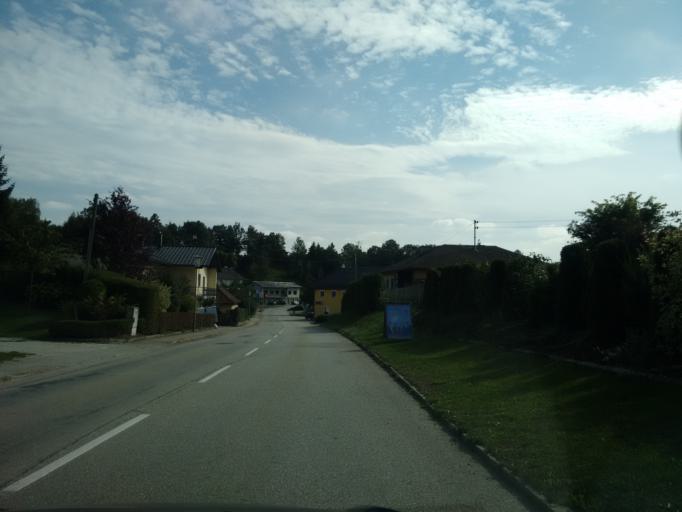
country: AT
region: Upper Austria
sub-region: Wels-Land
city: Marchtrenk
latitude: 48.1251
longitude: 14.0926
